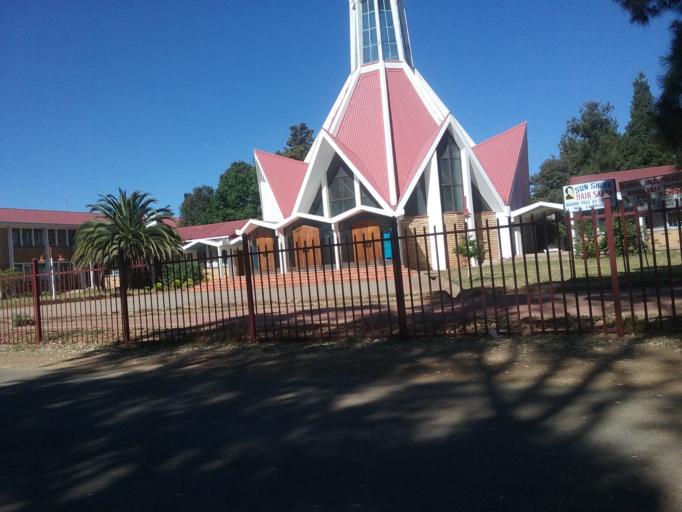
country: LS
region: Maseru
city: Nako
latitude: -29.4499
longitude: 27.7242
